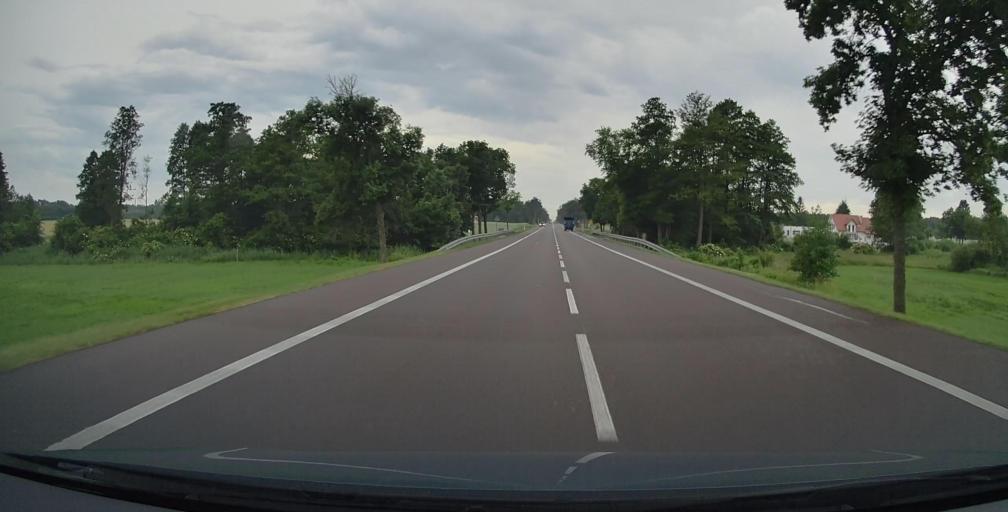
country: PL
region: Lublin Voivodeship
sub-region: Powiat bialski
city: Miedzyrzec Podlaski
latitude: 52.0170
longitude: 22.8467
